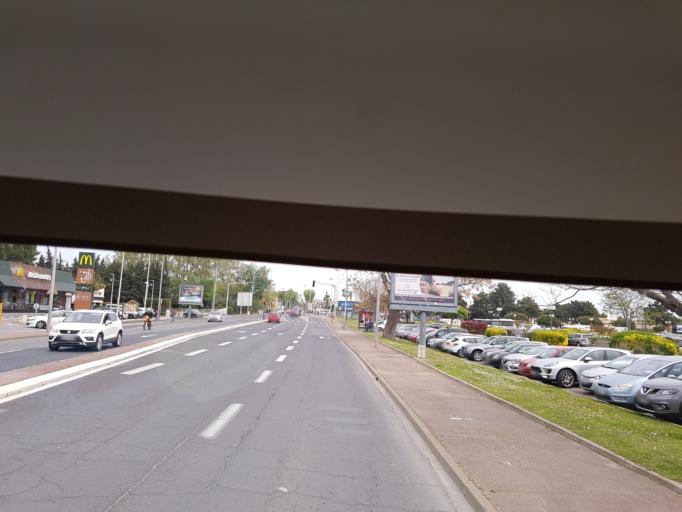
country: FR
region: Languedoc-Roussillon
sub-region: Departement de l'Aude
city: Narbonne
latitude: 43.1743
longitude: 2.9927
